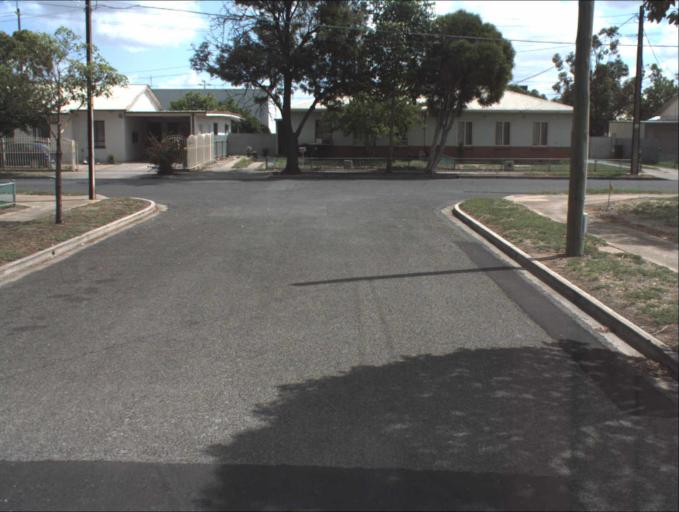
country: AU
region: South Australia
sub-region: Port Adelaide Enfield
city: Blair Athol
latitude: -34.8497
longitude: 138.5925
